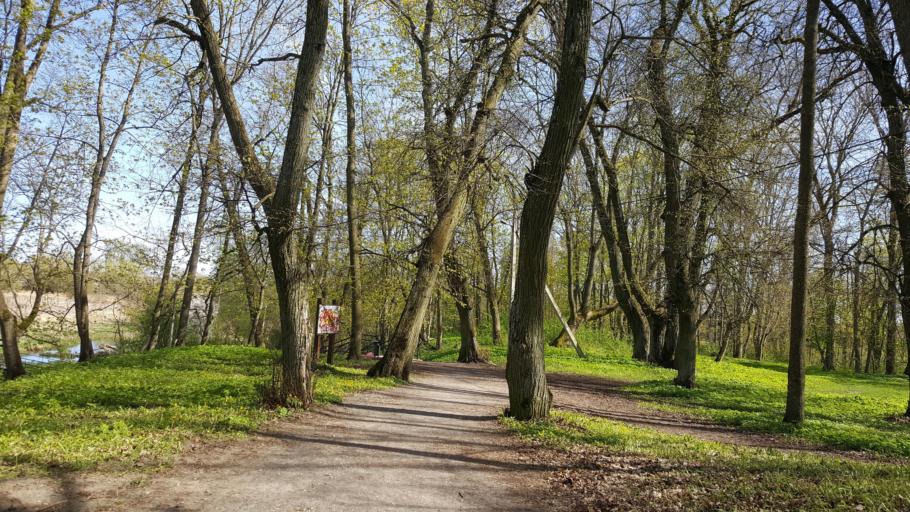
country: BY
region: Brest
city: Vysokaye
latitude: 52.3662
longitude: 23.3711
